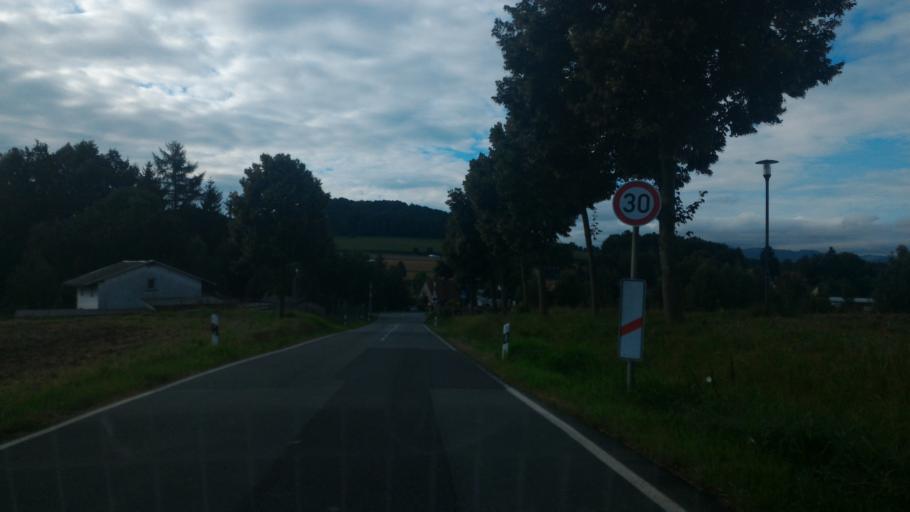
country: DE
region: Saxony
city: Leutersdorf
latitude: 50.9463
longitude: 14.6291
